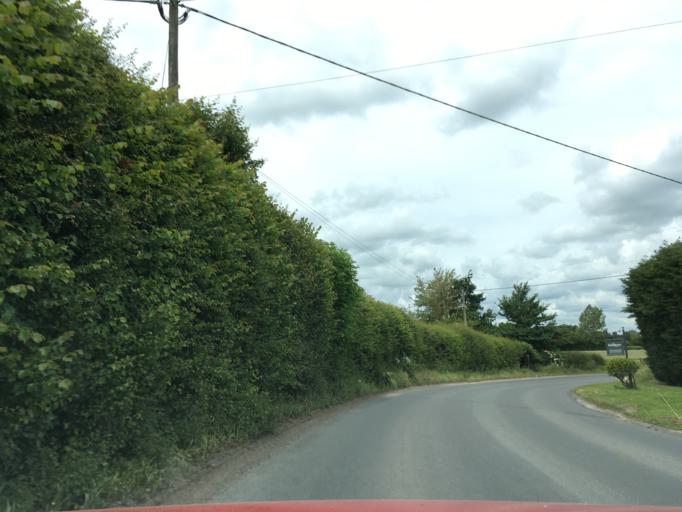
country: GB
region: England
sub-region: Wiltshire
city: Royal Wootton Bassett
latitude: 51.5653
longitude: -1.8898
